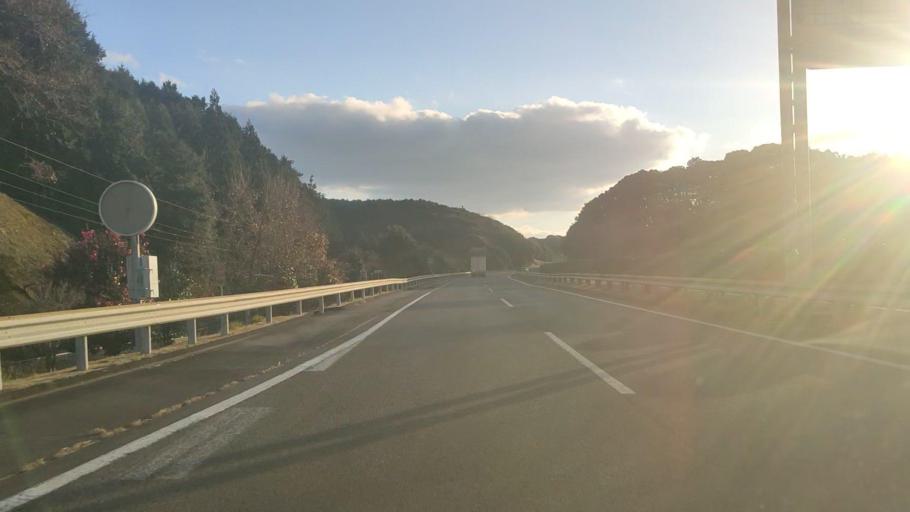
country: JP
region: Saga Prefecture
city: Ureshinomachi-shimojuku
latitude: 33.1429
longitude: 129.9966
